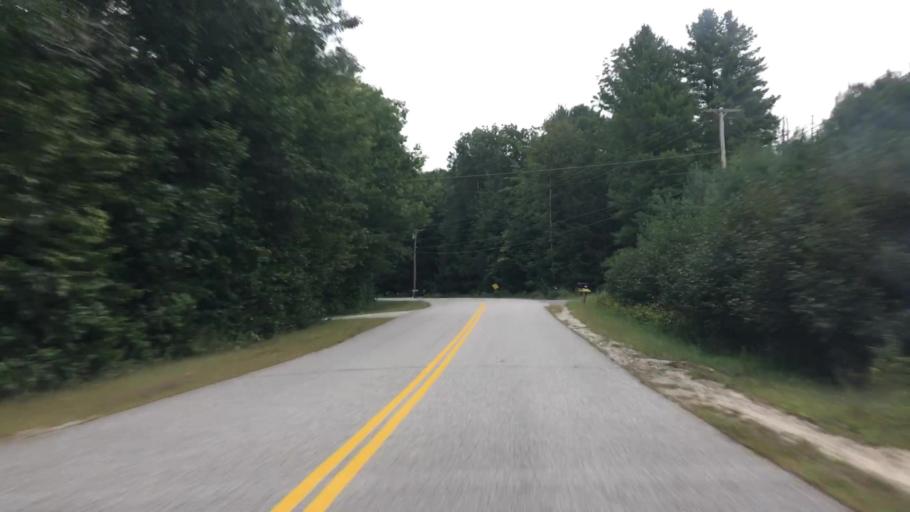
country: US
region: Maine
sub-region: Cumberland County
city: New Gloucester
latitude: 43.9214
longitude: -70.2596
